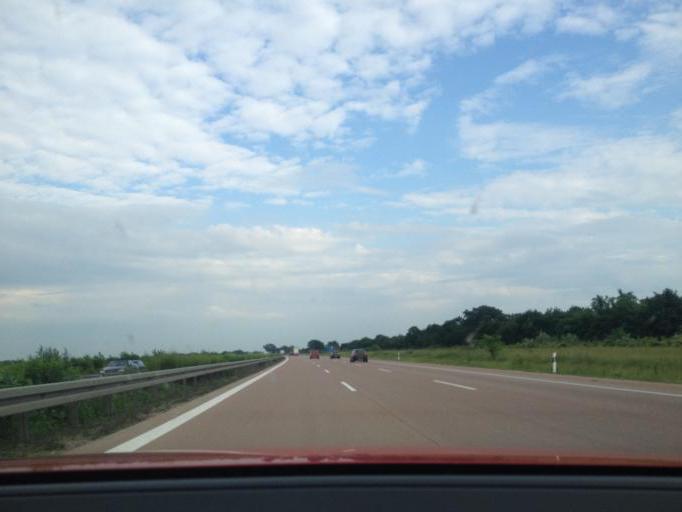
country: DE
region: Saxony-Anhalt
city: Grobers
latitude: 51.4623
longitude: 12.0971
